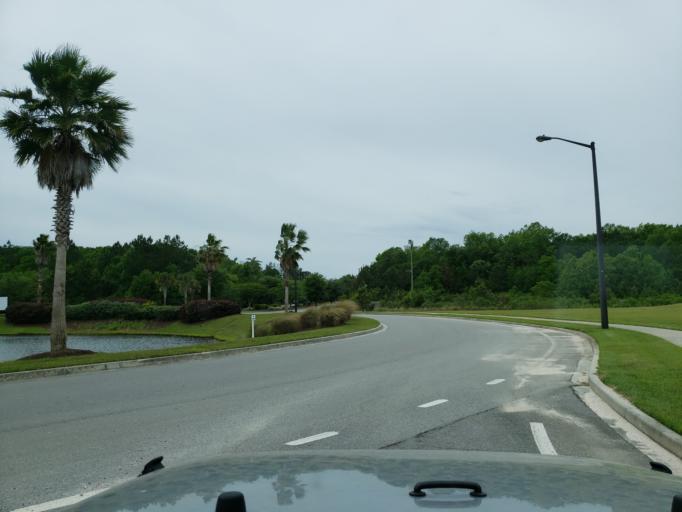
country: US
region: Georgia
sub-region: Chatham County
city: Port Wentworth
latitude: 32.2164
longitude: -81.1949
